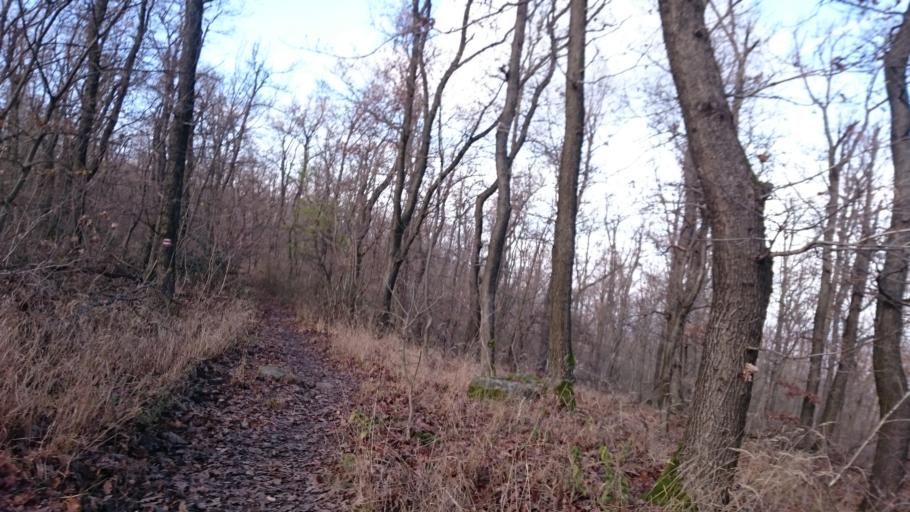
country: HU
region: Pest
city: Pilisborosjeno
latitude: 47.6129
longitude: 19.0041
